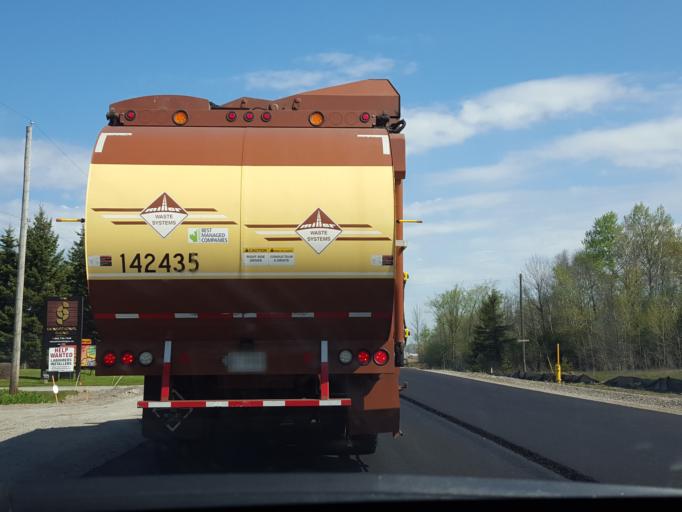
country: CA
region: Ontario
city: Uxbridge
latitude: 44.0715
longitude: -78.9351
